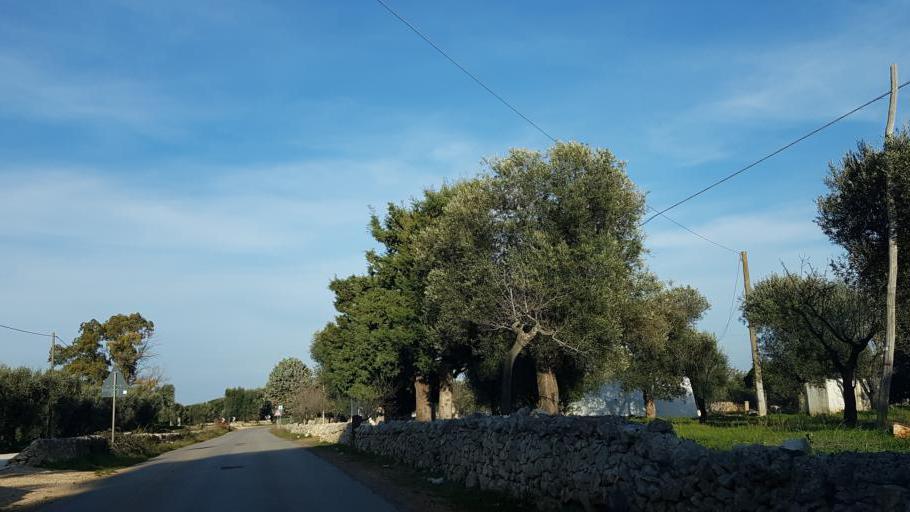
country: IT
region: Apulia
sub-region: Provincia di Brindisi
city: Carovigno
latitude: 40.7046
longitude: 17.6838
